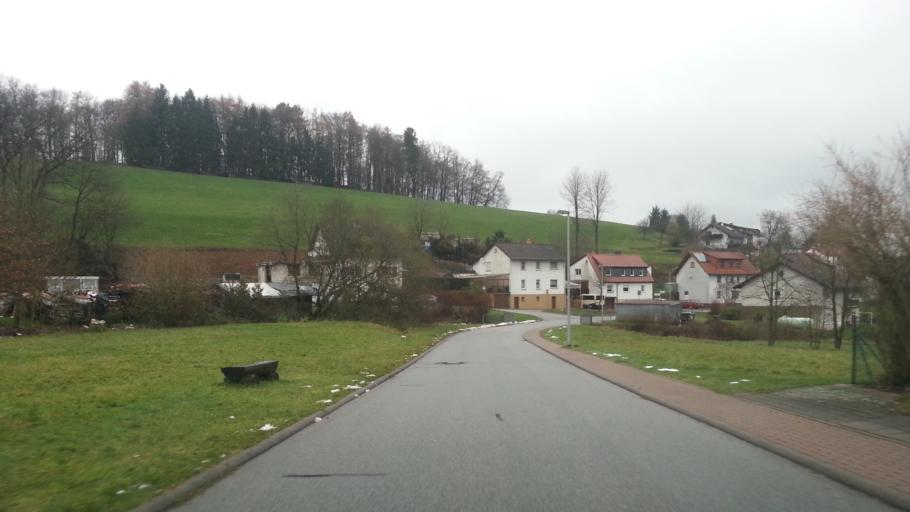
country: DE
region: Hesse
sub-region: Regierungsbezirk Darmstadt
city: Wald-Michelbach
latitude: 49.5628
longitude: 8.8290
